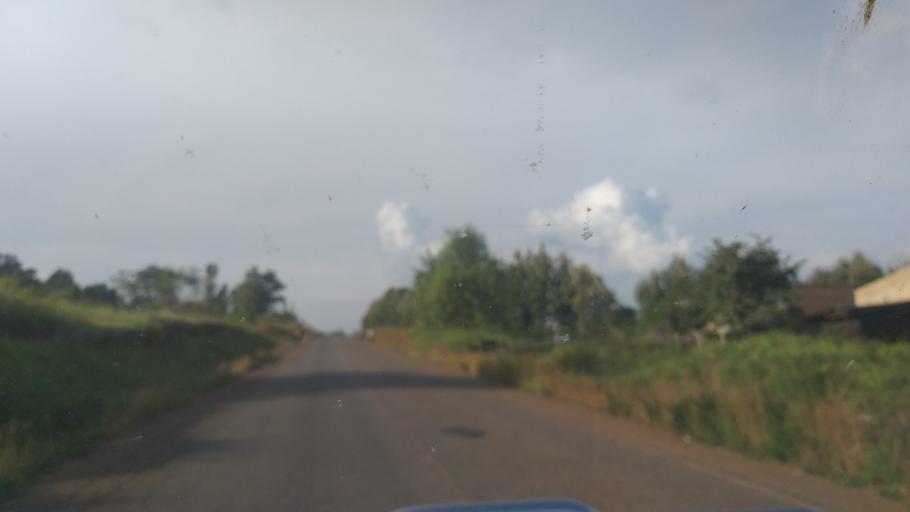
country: UG
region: Northern Region
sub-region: Arua District
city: Arua
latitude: 2.8358
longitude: 30.9932
